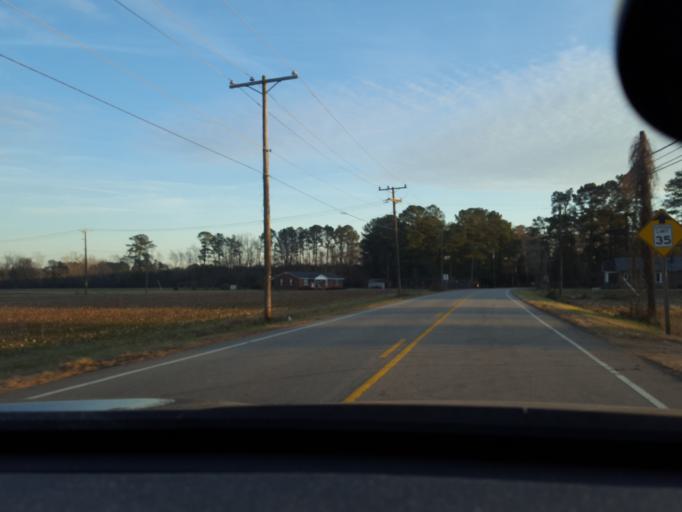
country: US
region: North Carolina
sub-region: Hertford County
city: Ahoskie
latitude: 36.2397
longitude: -77.1170
